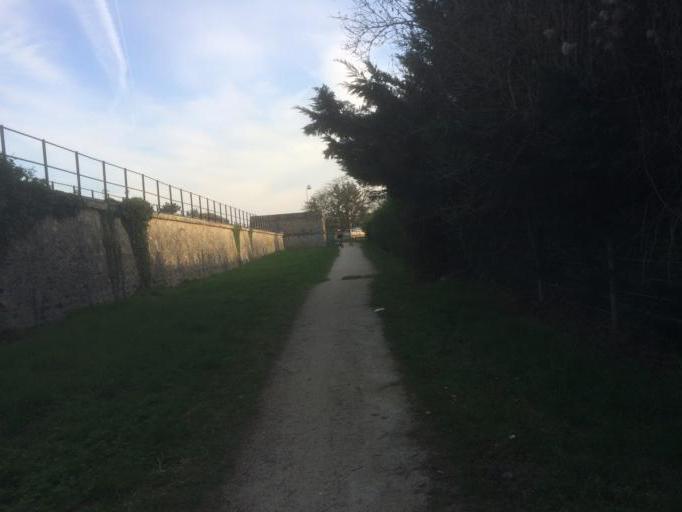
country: FR
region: Ile-de-France
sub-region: Departement de l'Essonne
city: Morsang-sur-Orge
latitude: 48.6621
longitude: 2.3733
